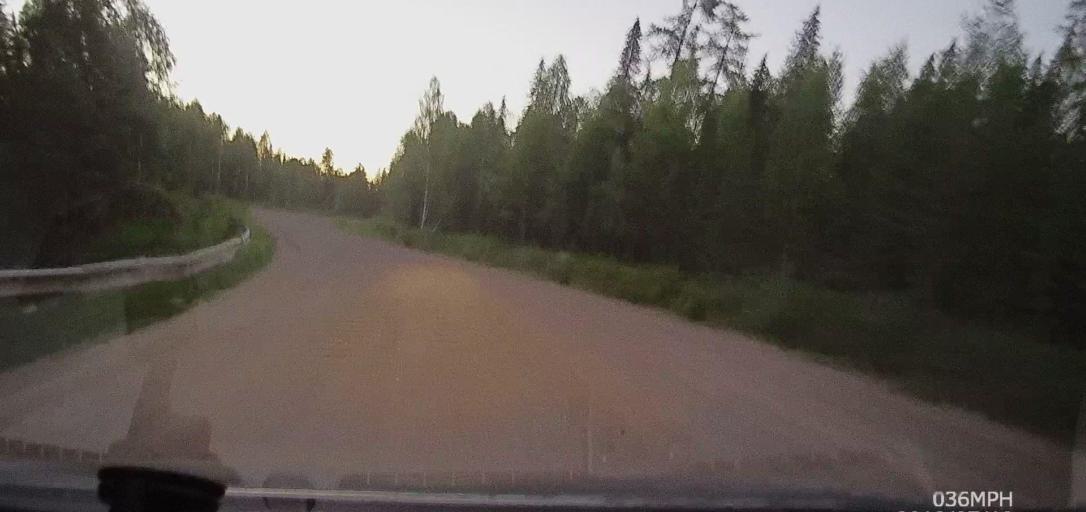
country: RU
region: Arkhangelskaya
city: Pinega
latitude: 64.4362
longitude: 43.1456
